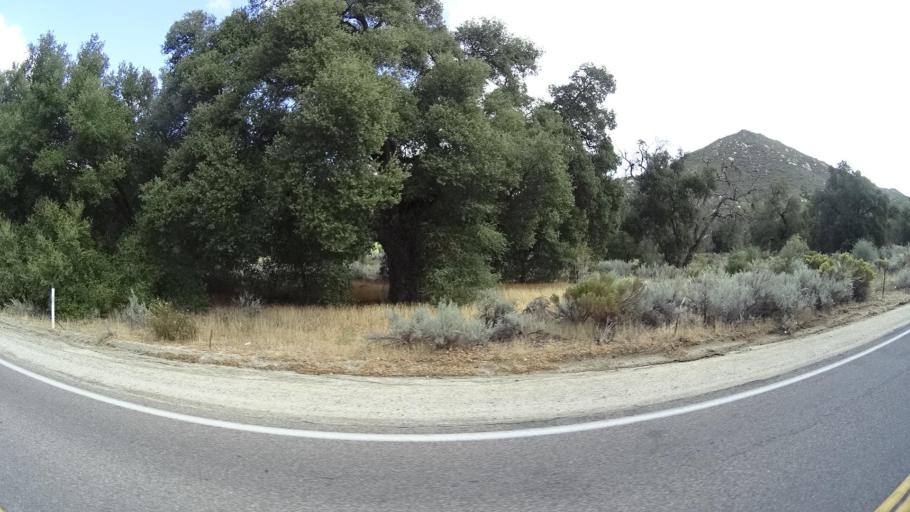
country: US
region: California
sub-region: San Diego County
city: Campo
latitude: 32.7000
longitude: -116.4889
